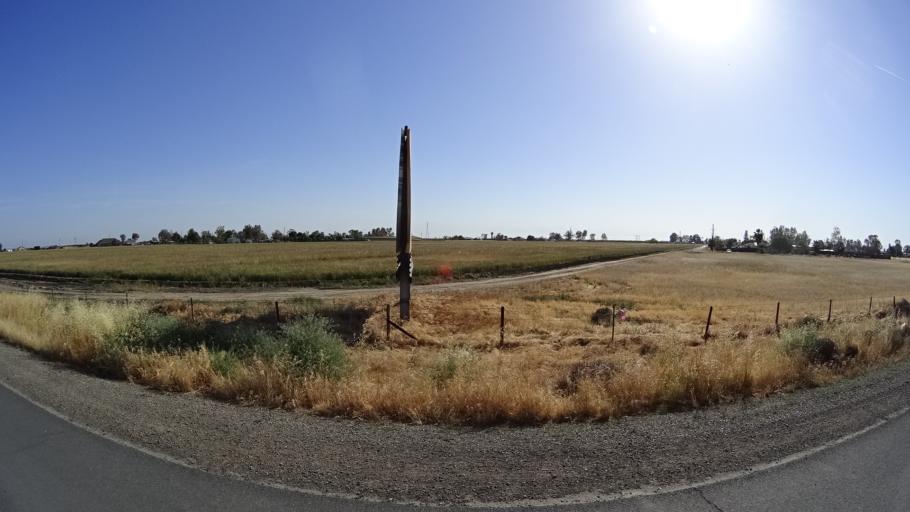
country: US
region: California
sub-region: Kings County
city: Corcoran
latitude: 36.1161
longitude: -119.5693
